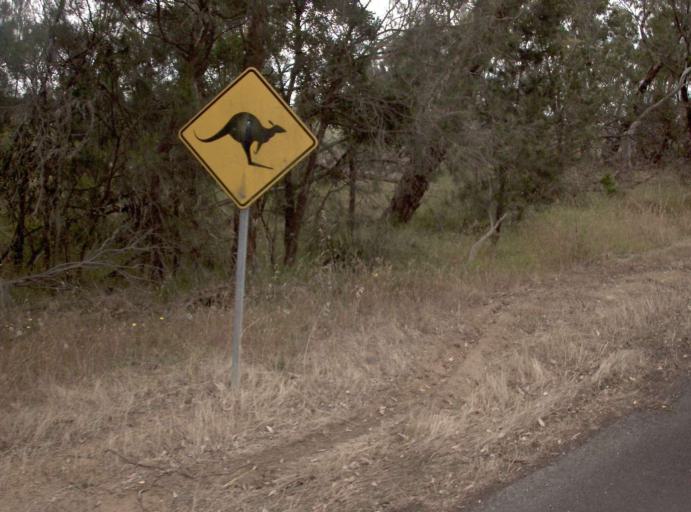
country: AU
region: Victoria
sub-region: Wellington
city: Sale
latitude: -38.3833
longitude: 146.9794
